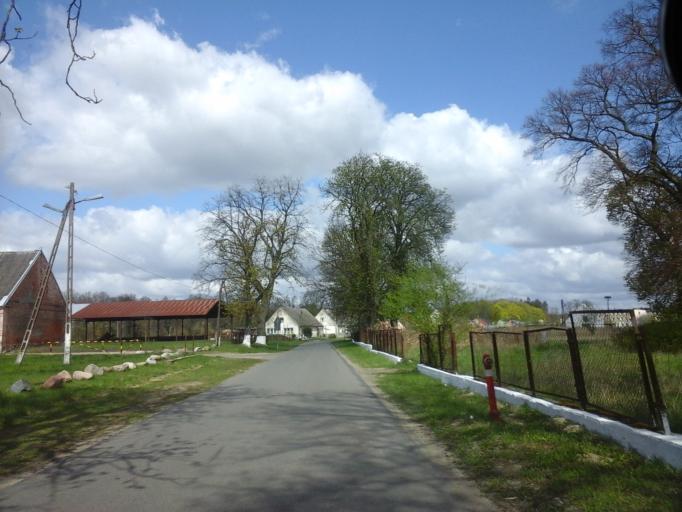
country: PL
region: West Pomeranian Voivodeship
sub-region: Powiat choszczenski
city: Bierzwnik
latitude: 53.1490
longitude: 15.6265
